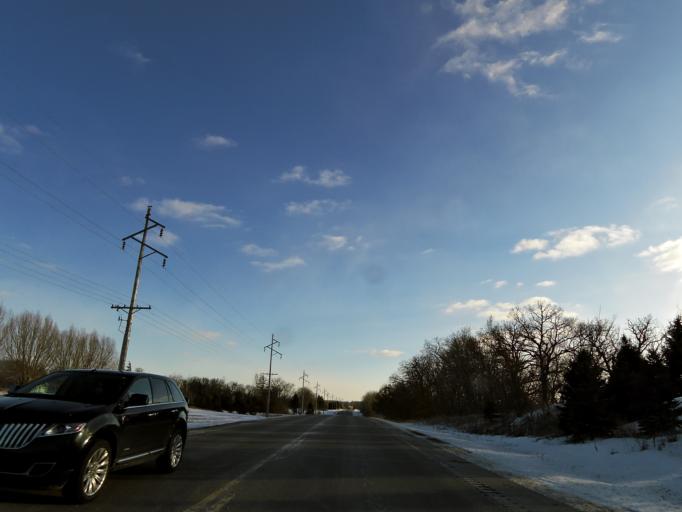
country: US
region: Minnesota
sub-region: Scott County
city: Prior Lake
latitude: 44.6780
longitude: -93.3387
